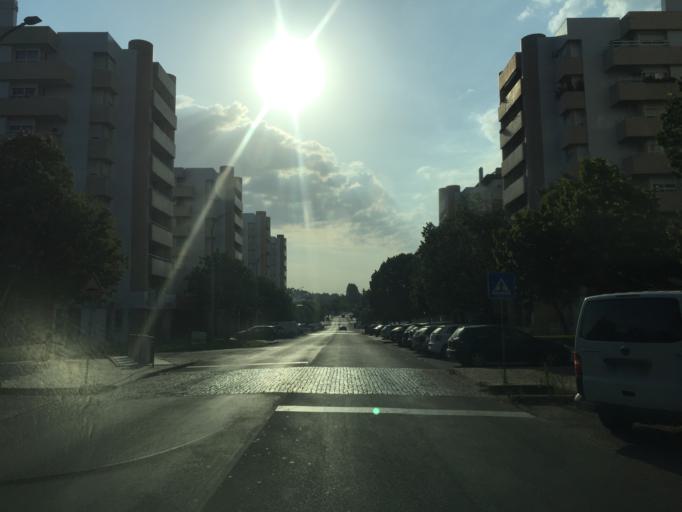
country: PT
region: Santarem
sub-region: Torres Novas
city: Torres Novas
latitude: 39.4732
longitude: -8.5424
